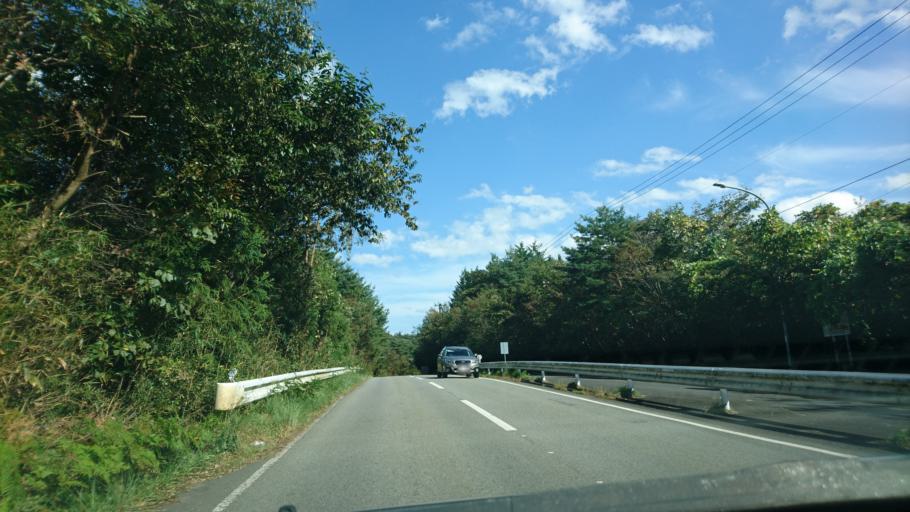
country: JP
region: Iwate
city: Ichinoseki
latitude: 38.8521
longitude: 141.0372
